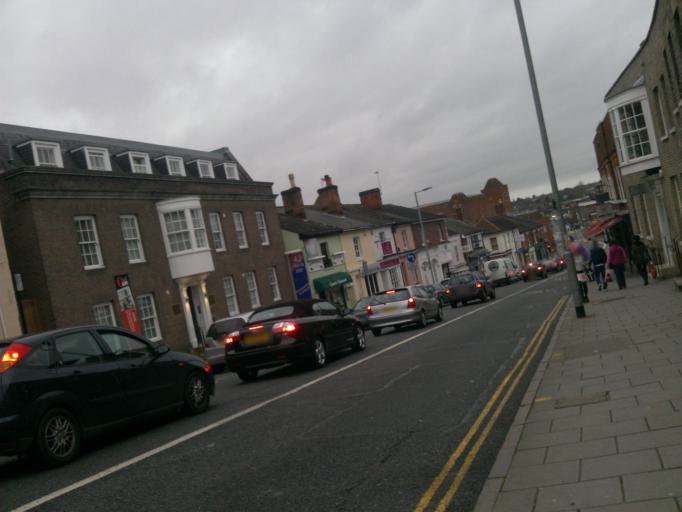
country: GB
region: England
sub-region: Essex
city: Colchester
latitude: 51.8911
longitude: 0.8961
